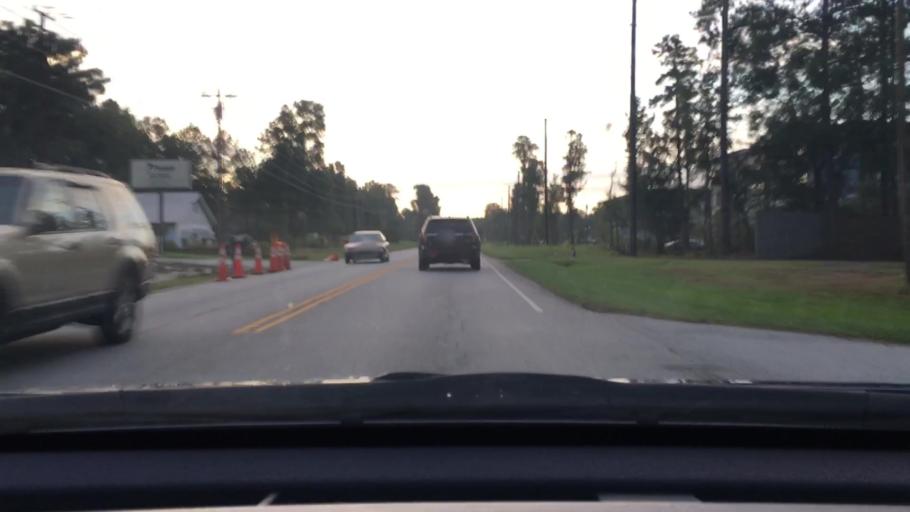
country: US
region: South Carolina
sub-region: Lexington County
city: Irmo
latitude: 34.0923
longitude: -81.1535
